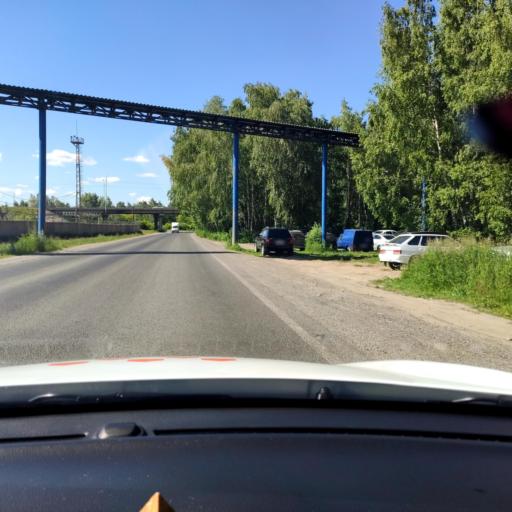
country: RU
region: Tatarstan
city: Staroye Arakchino
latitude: 55.8637
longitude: 48.9709
